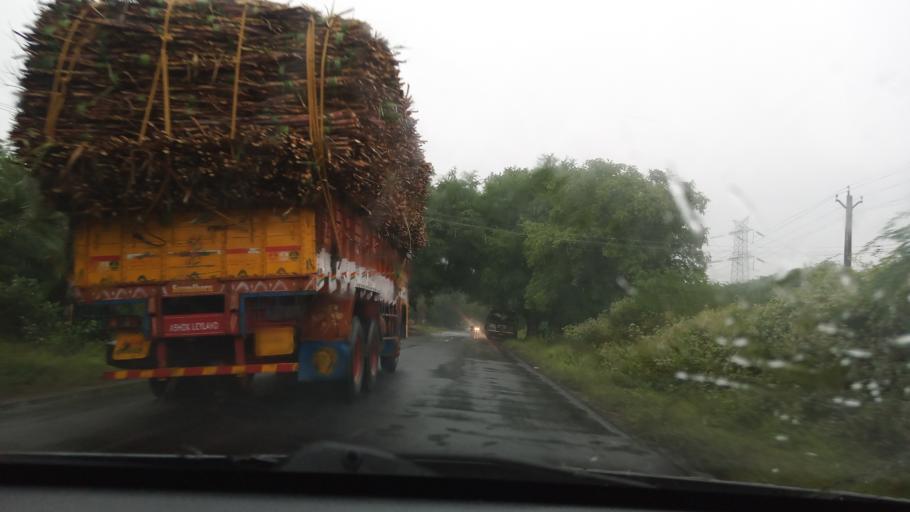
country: IN
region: Tamil Nadu
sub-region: Vellore
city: Walajapet
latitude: 12.8552
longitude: 79.3831
